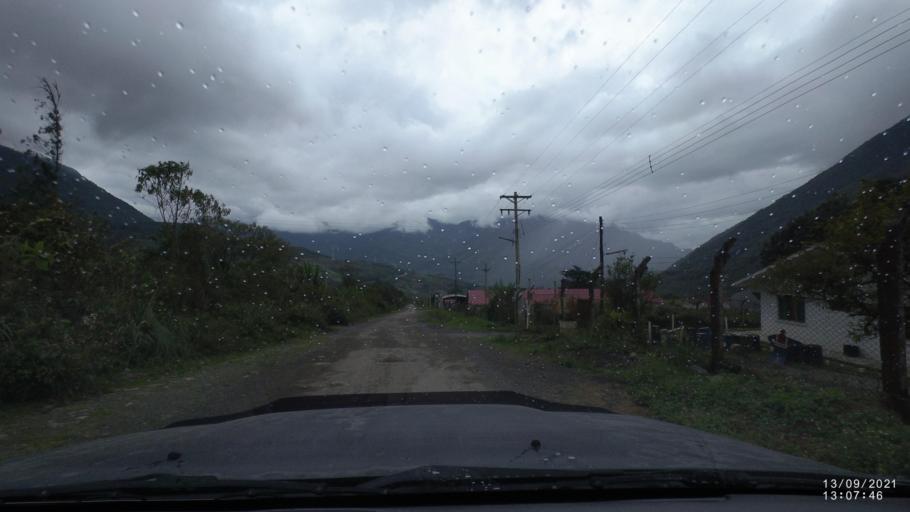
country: BO
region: Cochabamba
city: Colomi
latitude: -17.2191
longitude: -65.8225
